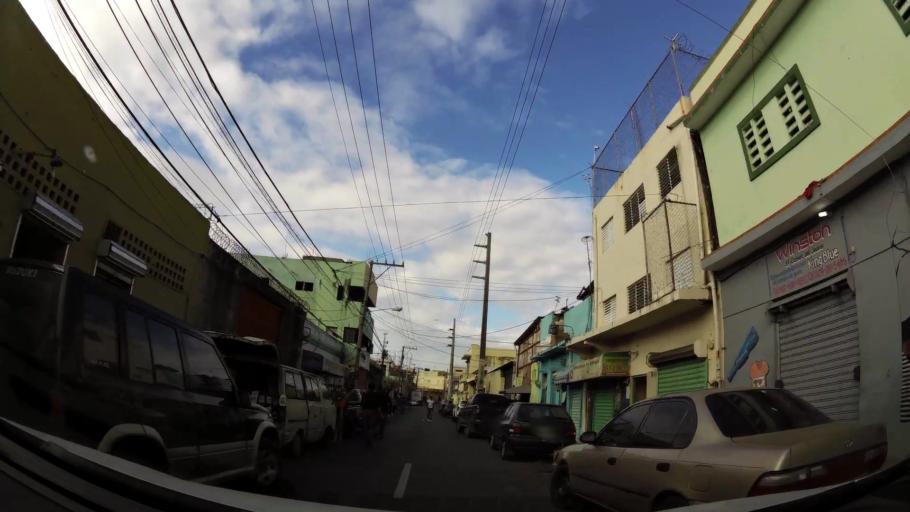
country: DO
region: Nacional
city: San Carlos
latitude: 18.4761
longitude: -69.8918
